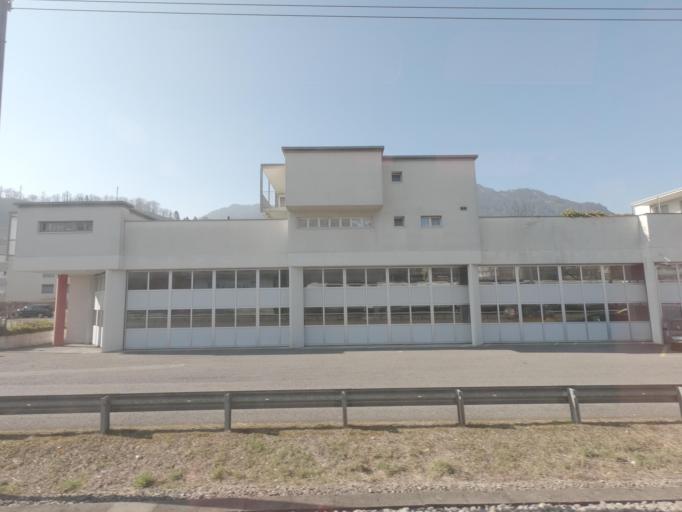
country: CH
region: Obwalden
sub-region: Obwalden
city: Sarnen
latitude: 46.9014
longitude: 8.2498
